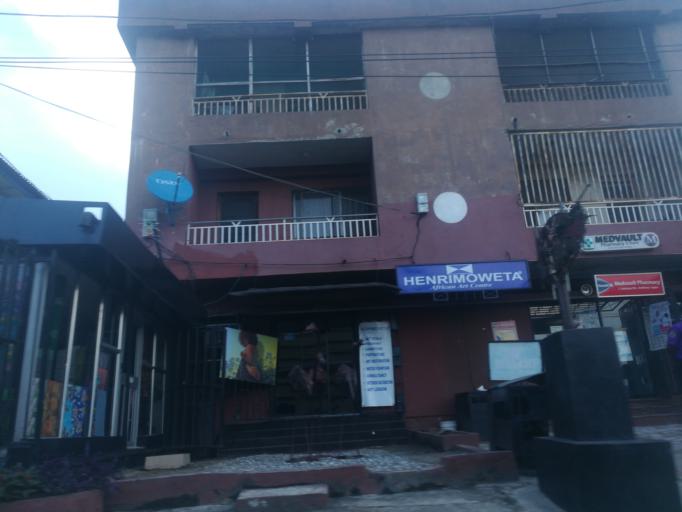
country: NG
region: Lagos
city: Somolu
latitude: 6.5579
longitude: 3.3708
